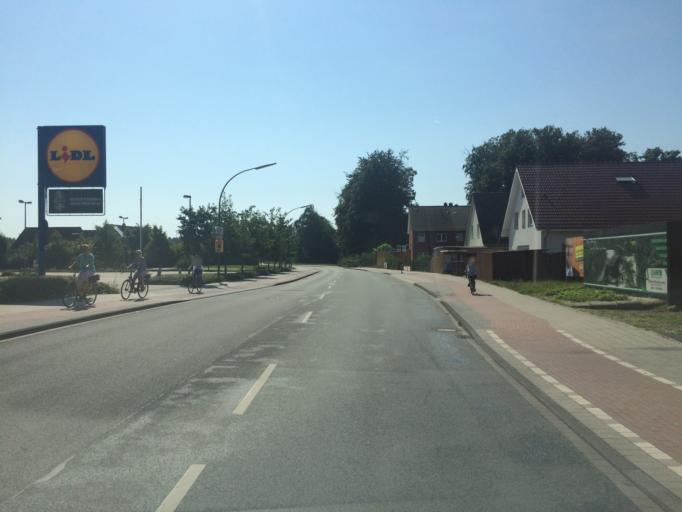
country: DE
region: North Rhine-Westphalia
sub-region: Regierungsbezirk Munster
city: Telgte
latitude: 51.9966
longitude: 7.7108
